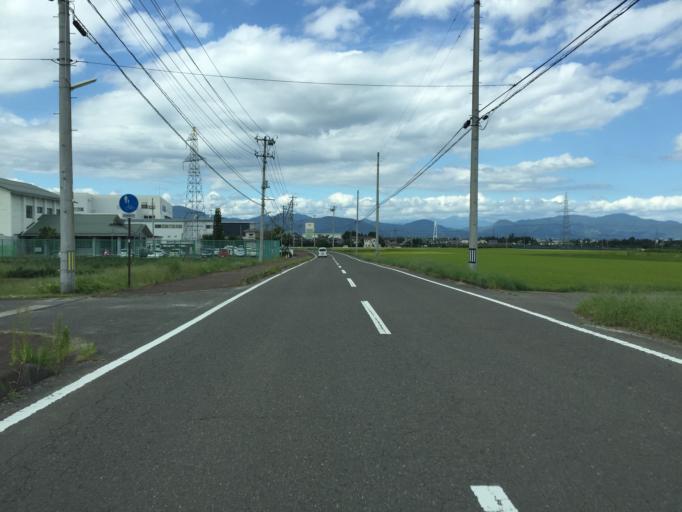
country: JP
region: Fukushima
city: Fukushima-shi
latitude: 37.7388
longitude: 140.4080
